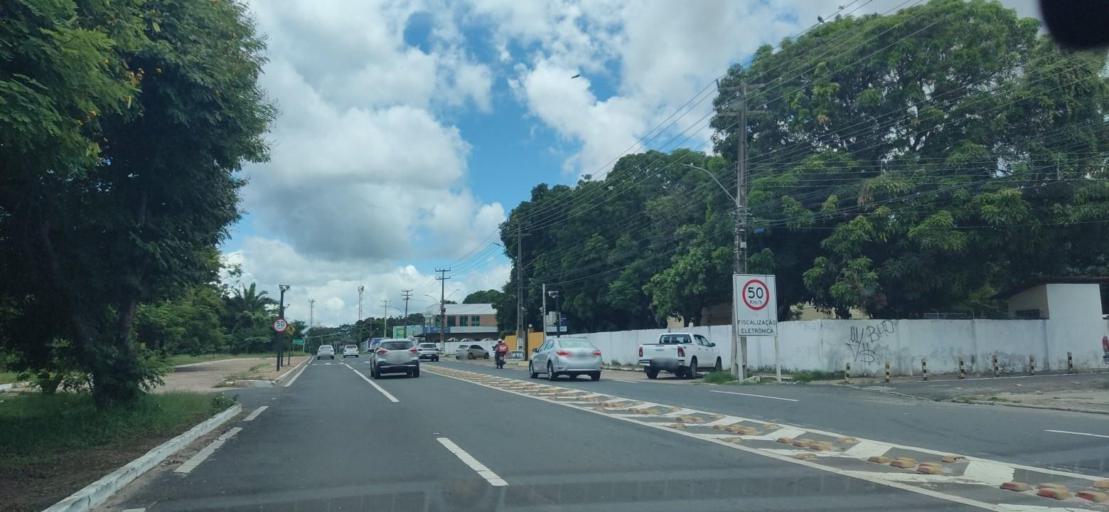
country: BR
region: Piaui
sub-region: Teresina
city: Teresina
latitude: -5.0815
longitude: -42.7745
